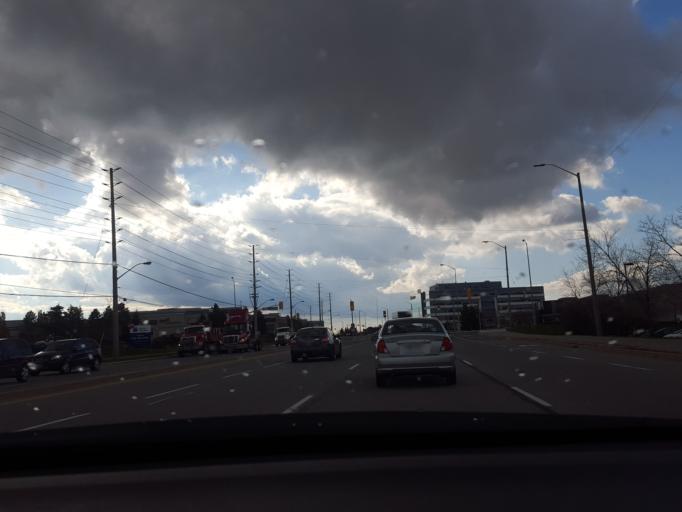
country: CA
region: Ontario
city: Brampton
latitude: 43.6124
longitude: -79.7479
